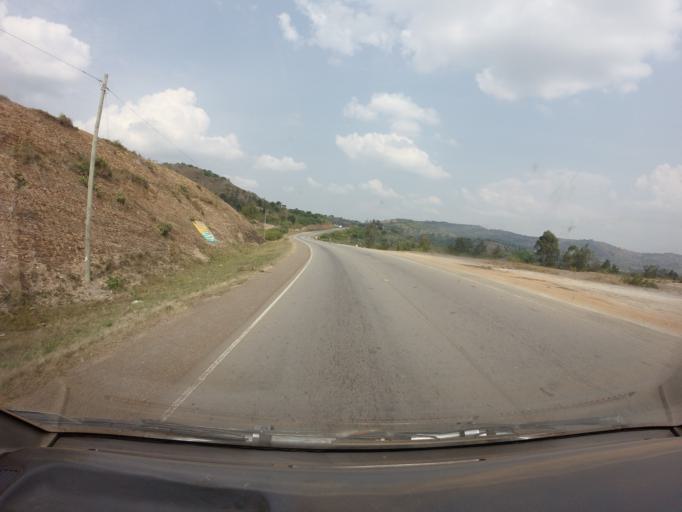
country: UG
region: Central Region
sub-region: Lyantonde District
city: Lyantonde
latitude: -0.3741
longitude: 31.2759
